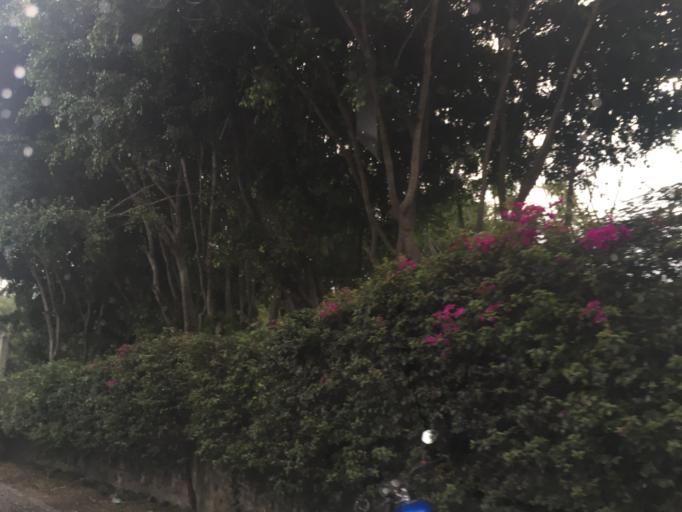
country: GT
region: Sacatepequez
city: Antigua Guatemala
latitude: 14.5609
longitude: -90.7406
